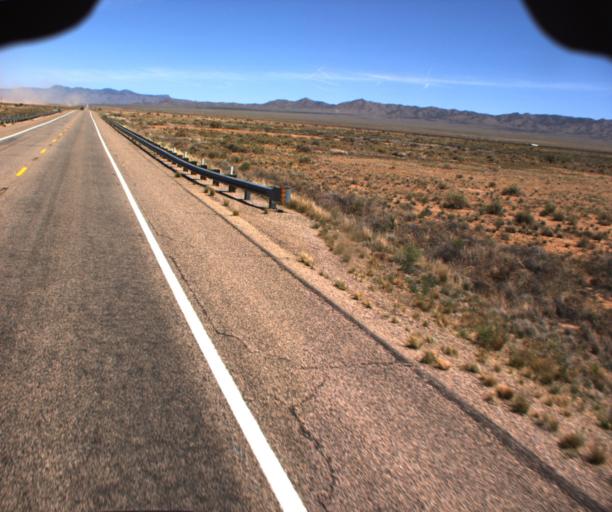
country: US
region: Arizona
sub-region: Mohave County
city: New Kingman-Butler
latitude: 35.3188
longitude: -113.9136
